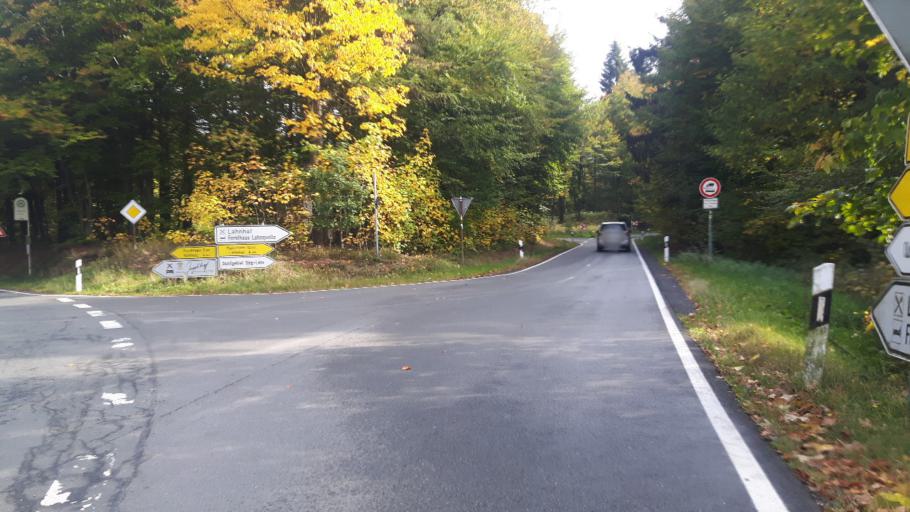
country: DE
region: North Rhine-Westphalia
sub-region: Regierungsbezirk Arnsberg
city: Erndtebruck
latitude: 50.9192
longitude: 8.2450
